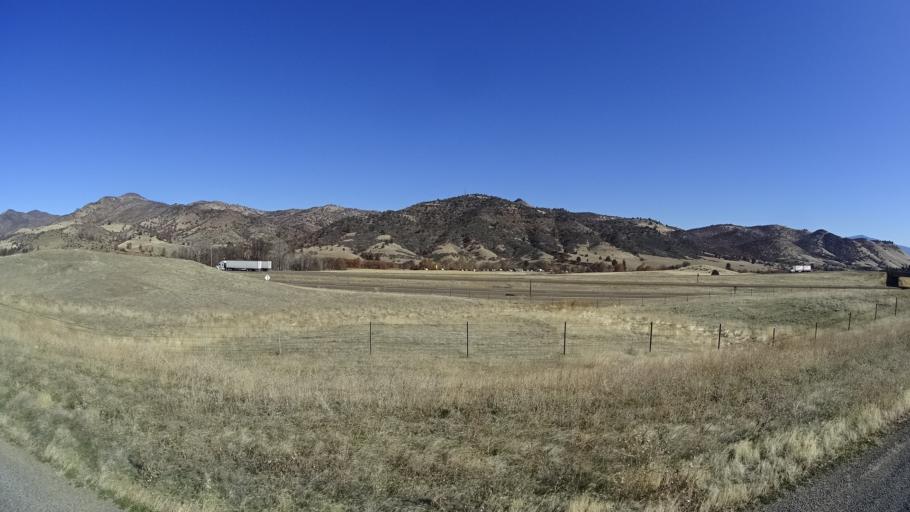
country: US
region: California
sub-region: Siskiyou County
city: Yreka
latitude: 41.9210
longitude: -122.5770
